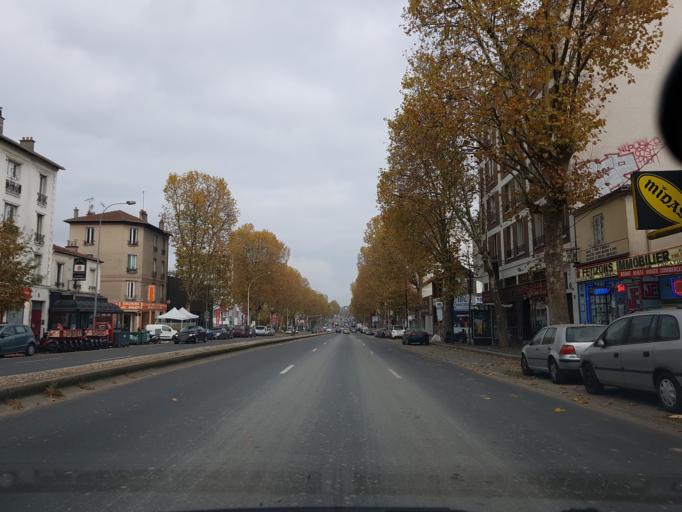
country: FR
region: Ile-de-France
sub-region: Departement du Val-de-Marne
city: Arcueil
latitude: 48.7968
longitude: 2.3221
